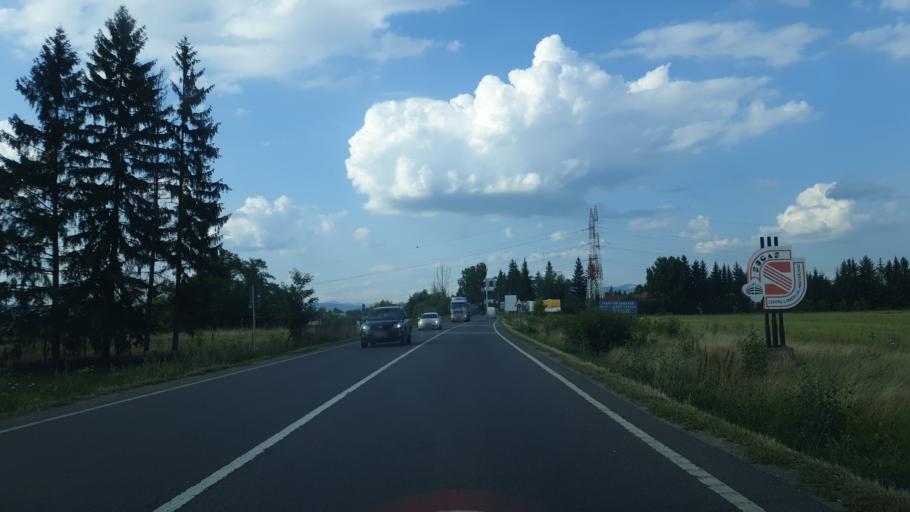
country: RO
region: Covasna
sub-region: Municipiul Sfantu Gheorghe
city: Sfantu-Gheorghe
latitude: 45.8452
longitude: 25.8043
